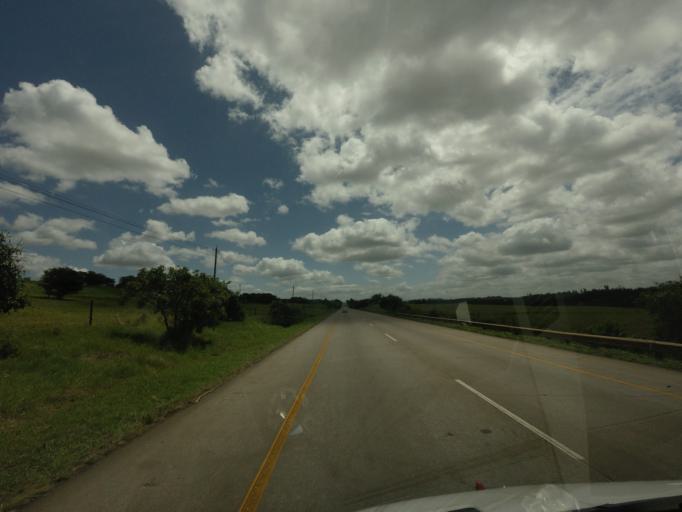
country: ZA
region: KwaZulu-Natal
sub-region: uMkhanyakude District Municipality
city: Mtubatuba
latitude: -28.4856
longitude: 32.1422
